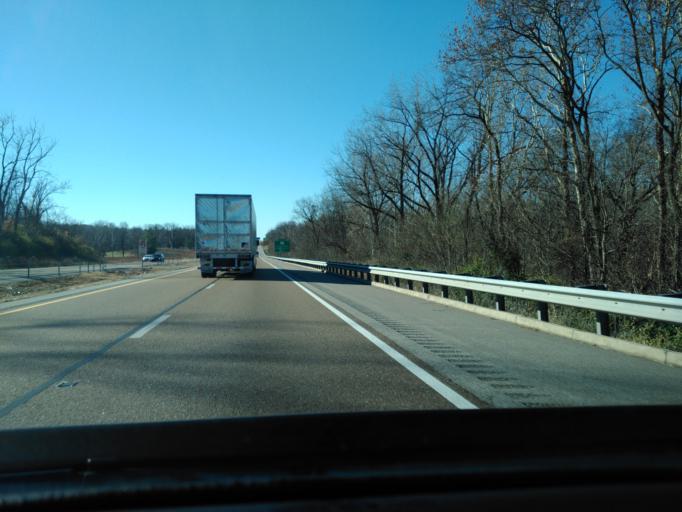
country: US
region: Illinois
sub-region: Madison County
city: Collinsville
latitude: 38.6927
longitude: -89.9993
